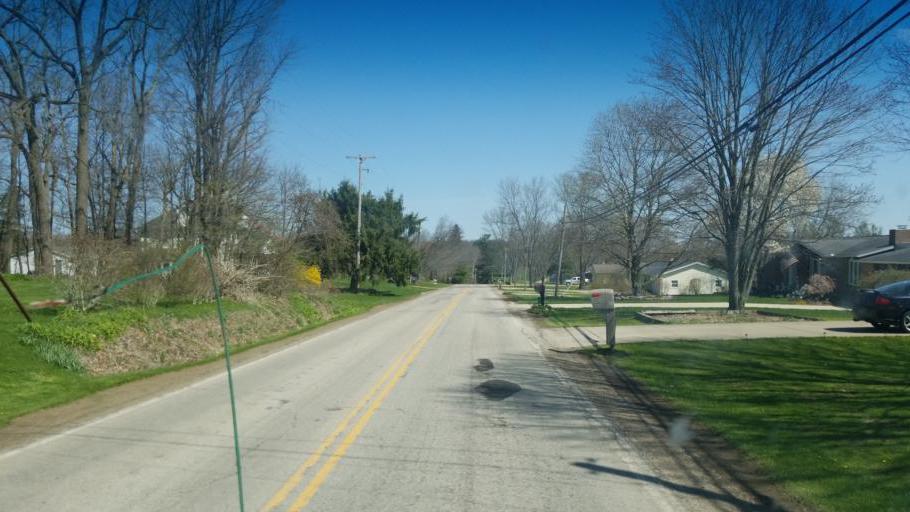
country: US
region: Ohio
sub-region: Richland County
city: Lincoln Heights
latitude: 40.7978
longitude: -82.4441
